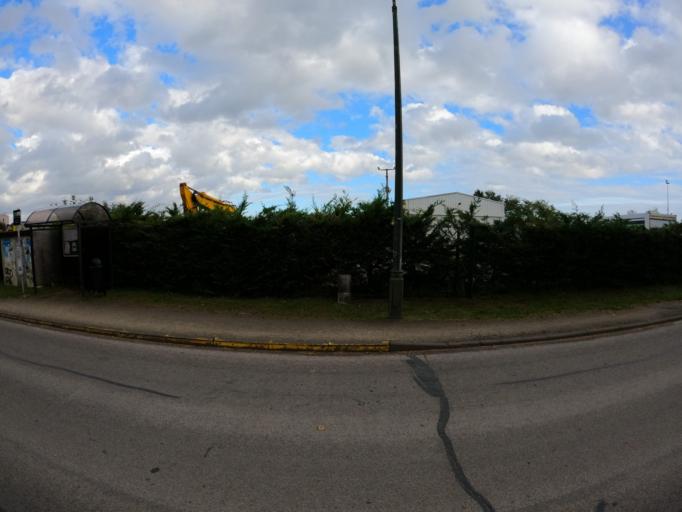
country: FR
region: Ile-de-France
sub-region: Departement de Seine-et-Marne
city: Esbly
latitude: 48.9149
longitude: 2.8146
